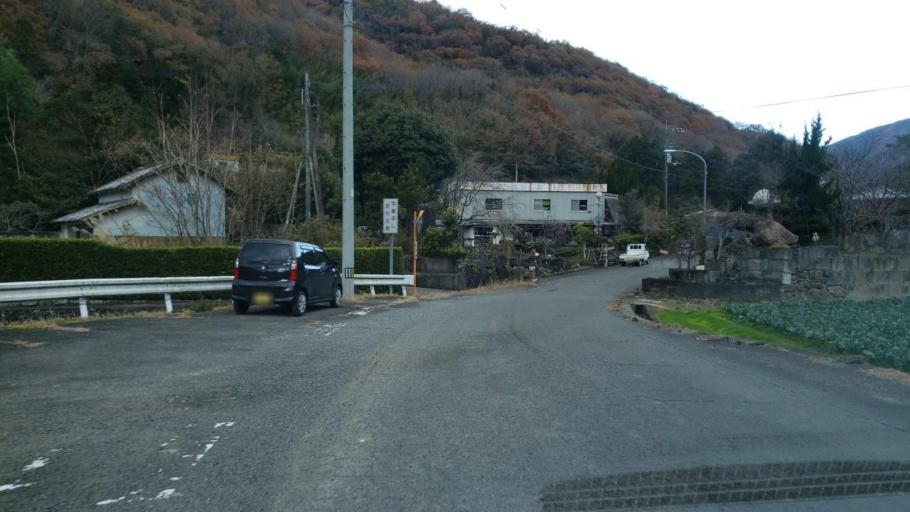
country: JP
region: Tokushima
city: Wakimachi
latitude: 34.1115
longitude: 134.2240
